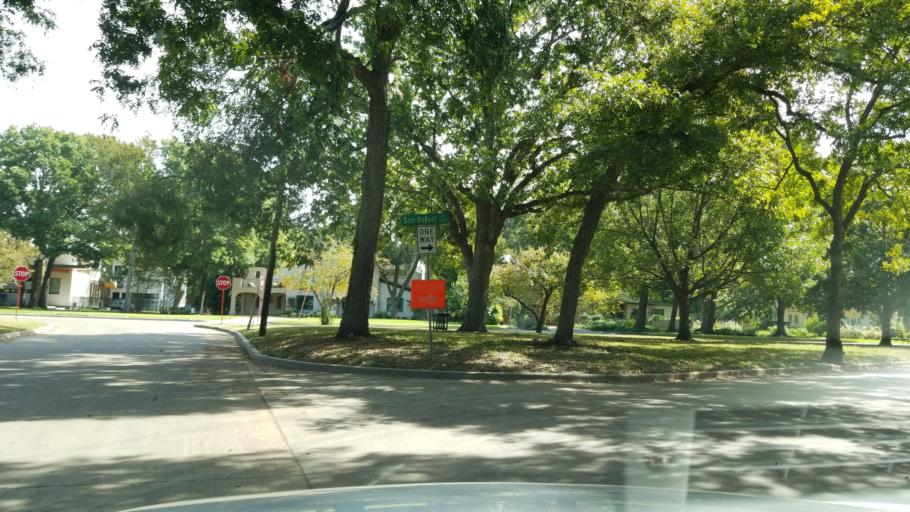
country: US
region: Texas
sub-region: Dallas County
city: Highland Park
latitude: 32.8119
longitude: -96.7212
